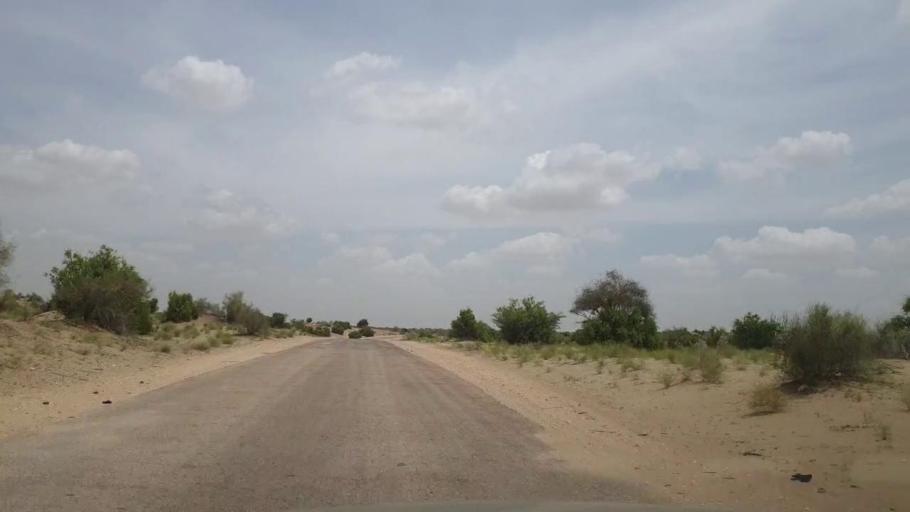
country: PK
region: Sindh
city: Kot Diji
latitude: 27.1885
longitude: 69.1693
